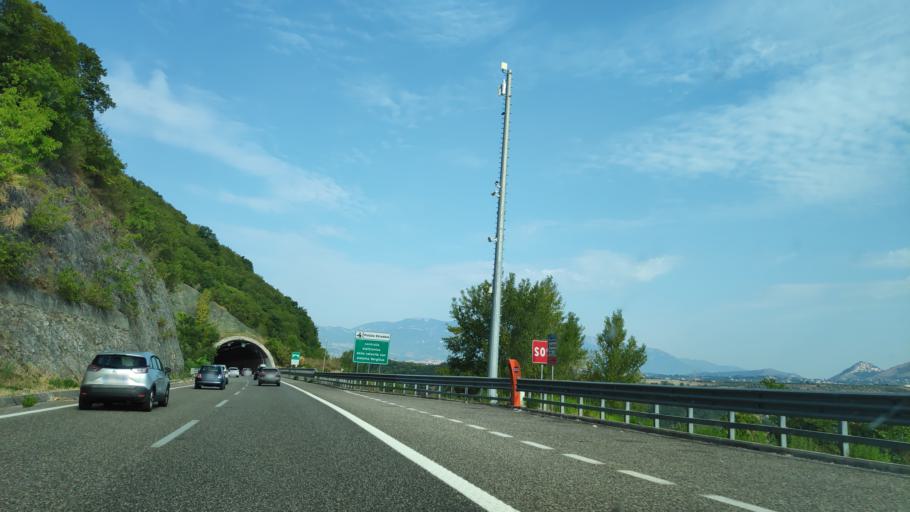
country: IT
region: Campania
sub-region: Provincia di Salerno
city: Sicignano degli Alburni
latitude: 40.5998
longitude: 15.3119
